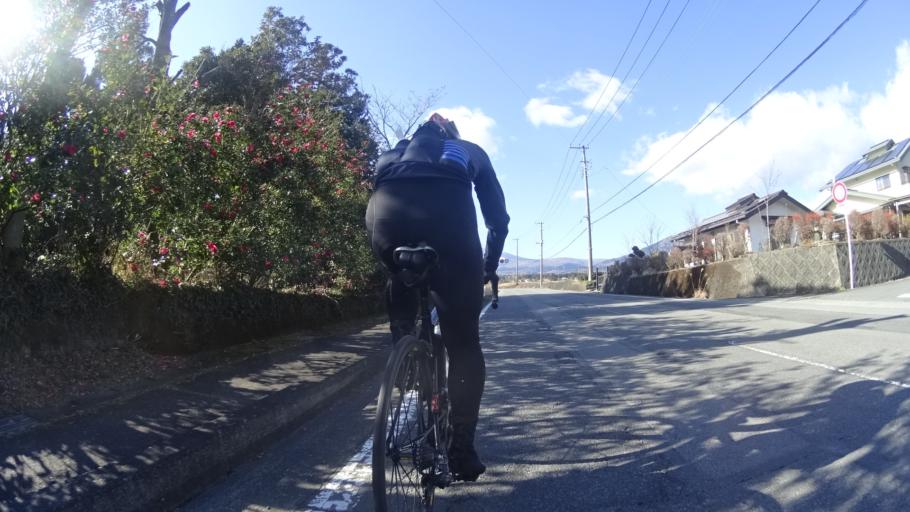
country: JP
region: Shizuoka
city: Gotemba
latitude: 35.3380
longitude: 138.9329
